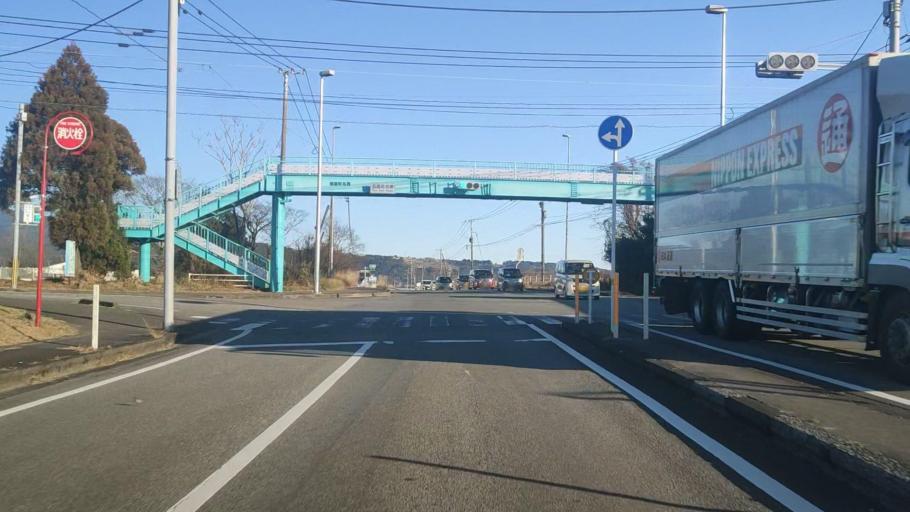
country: JP
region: Miyazaki
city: Takanabe
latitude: 32.2464
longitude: 131.5517
